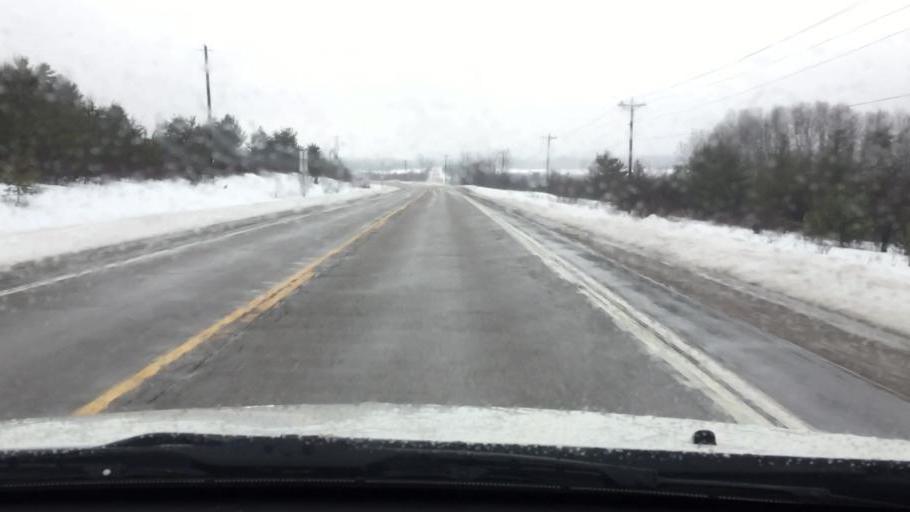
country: US
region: Michigan
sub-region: Charlevoix County
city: East Jordan
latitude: 45.1161
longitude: -85.1294
